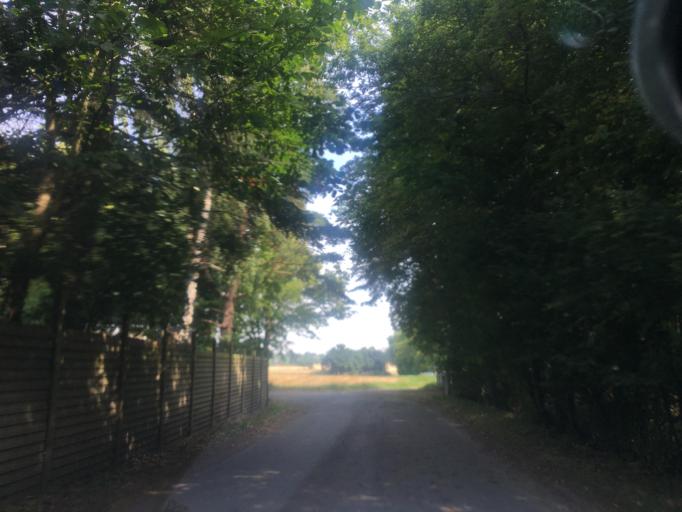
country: DK
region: Zealand
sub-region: Vordingborg Kommune
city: Praesto
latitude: 55.1836
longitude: 12.0777
